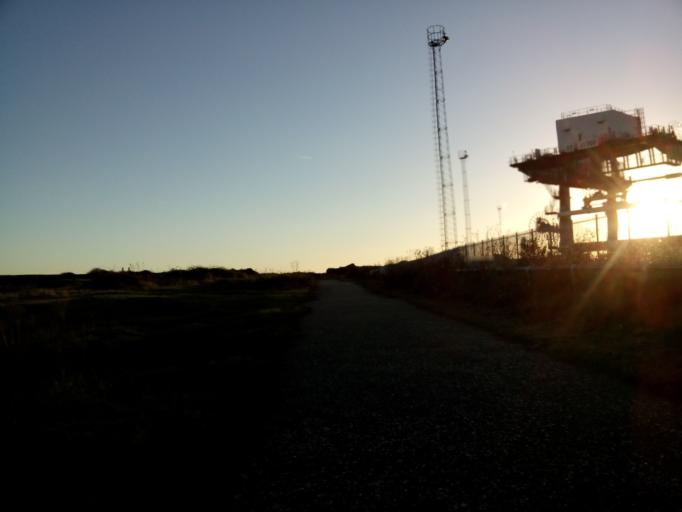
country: GB
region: England
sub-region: Suffolk
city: Felixstowe
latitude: 51.9419
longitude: 1.3266
